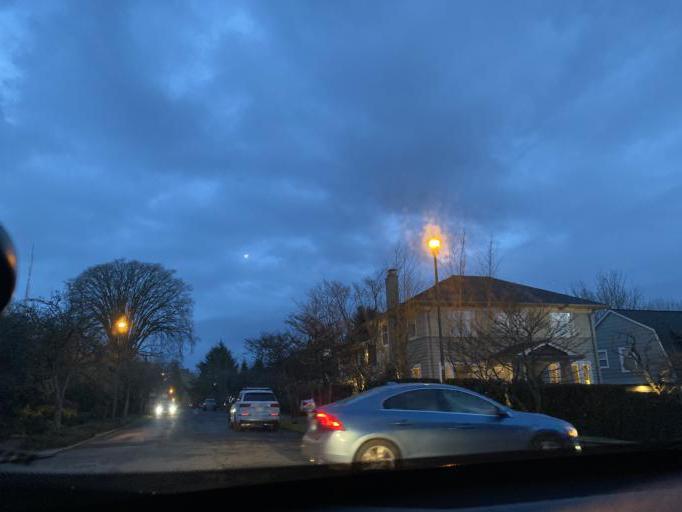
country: US
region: Washington
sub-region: King County
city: Seattle
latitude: 47.6305
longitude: -122.3633
